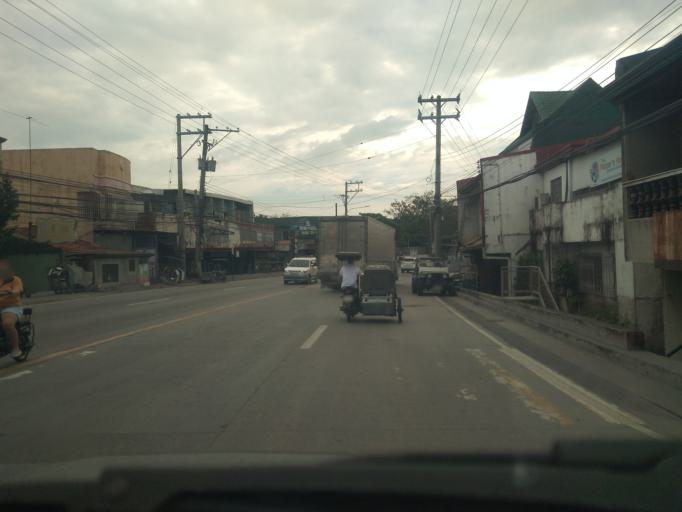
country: PH
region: Central Luzon
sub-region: Province of Pampanga
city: Del Pilar
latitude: 15.0327
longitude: 120.6949
